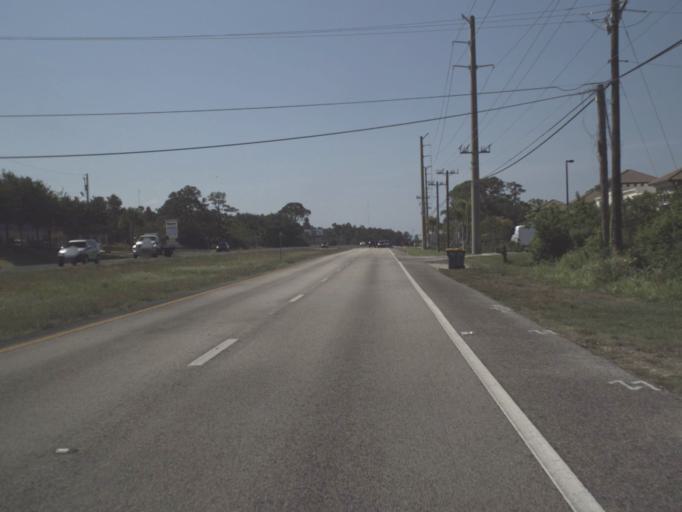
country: US
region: Florida
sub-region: Brevard County
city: South Patrick Shores
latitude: 28.2547
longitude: -80.6845
